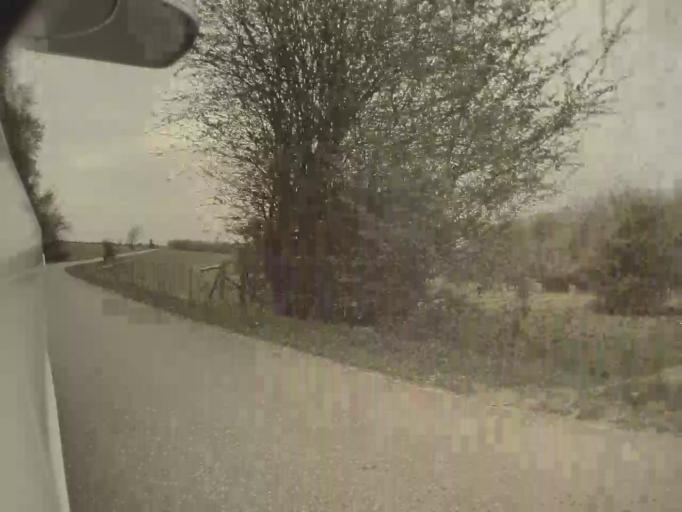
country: BE
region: Wallonia
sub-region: Province du Luxembourg
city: La Roche-en-Ardenne
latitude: 50.2291
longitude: 5.6138
